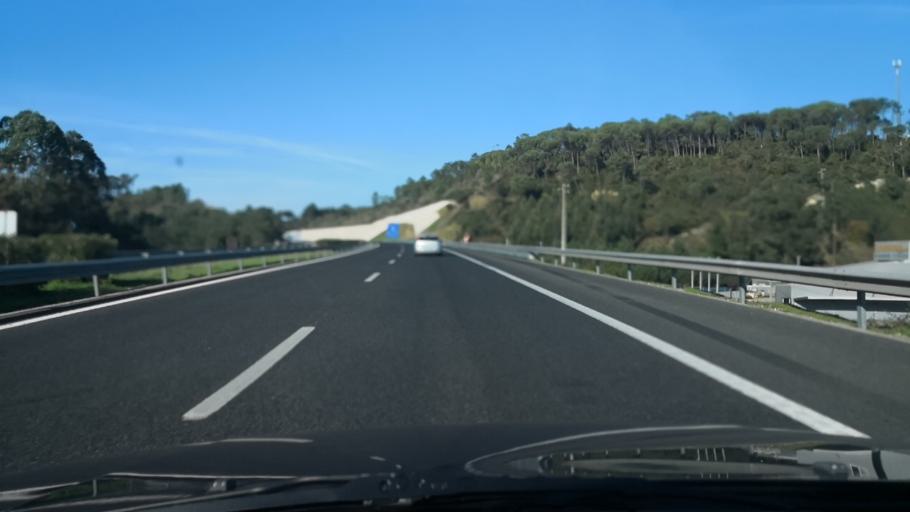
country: PT
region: Leiria
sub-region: Leiria
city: Caranguejeira
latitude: 39.7233
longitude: -8.7152
